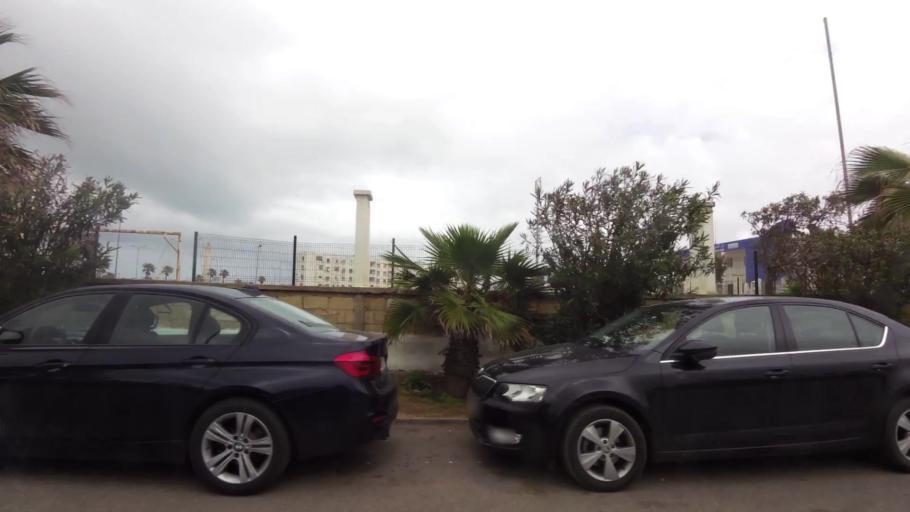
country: MA
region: Grand Casablanca
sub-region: Casablanca
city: Casablanca
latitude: 33.6053
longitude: -7.6570
